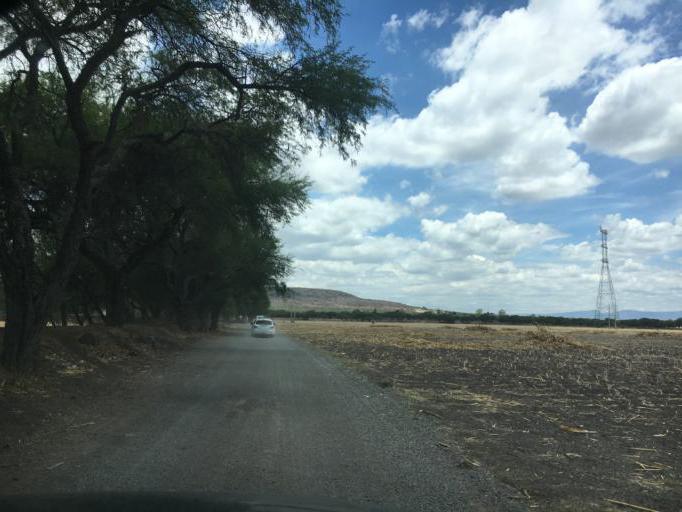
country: MX
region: Guanajuato
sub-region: Leon
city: Plan Guanajuato (La Sandia)
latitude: 20.9214
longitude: -101.7493
